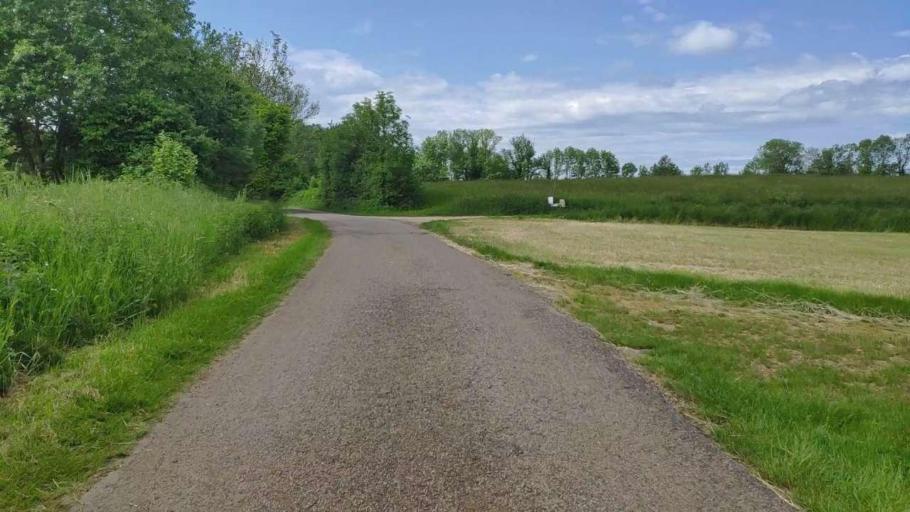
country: FR
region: Franche-Comte
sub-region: Departement du Jura
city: Poligny
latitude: 46.7766
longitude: 5.6290
